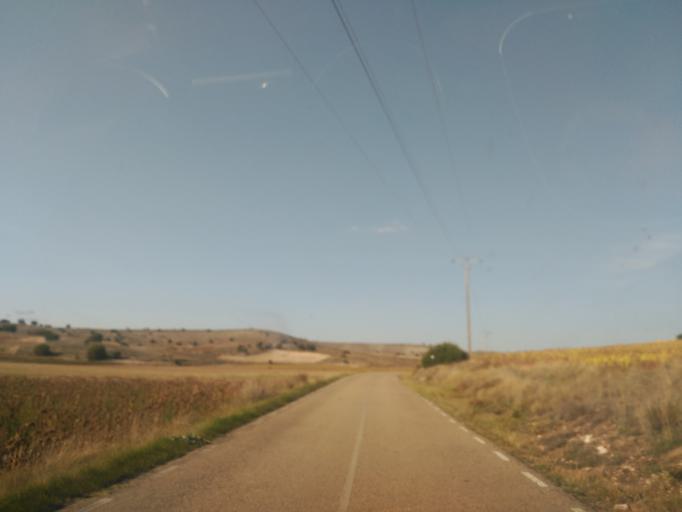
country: ES
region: Castille and Leon
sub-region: Provincia de Burgos
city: Penaranda de Duero
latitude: 41.6409
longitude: -3.4872
